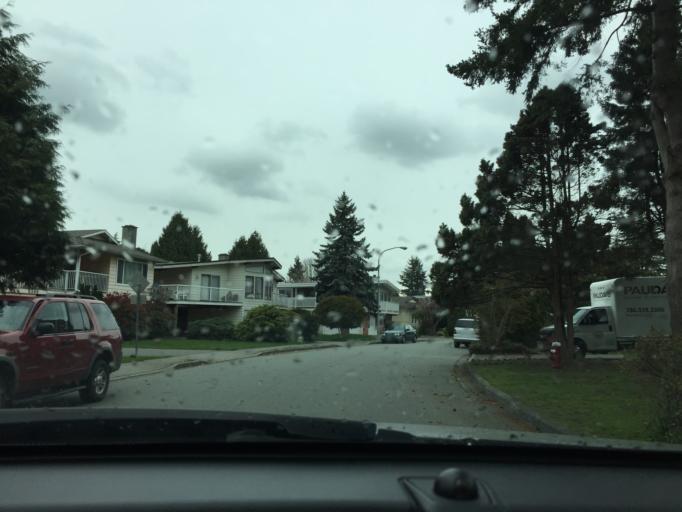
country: CA
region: British Columbia
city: Richmond
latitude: 49.1463
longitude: -123.1305
